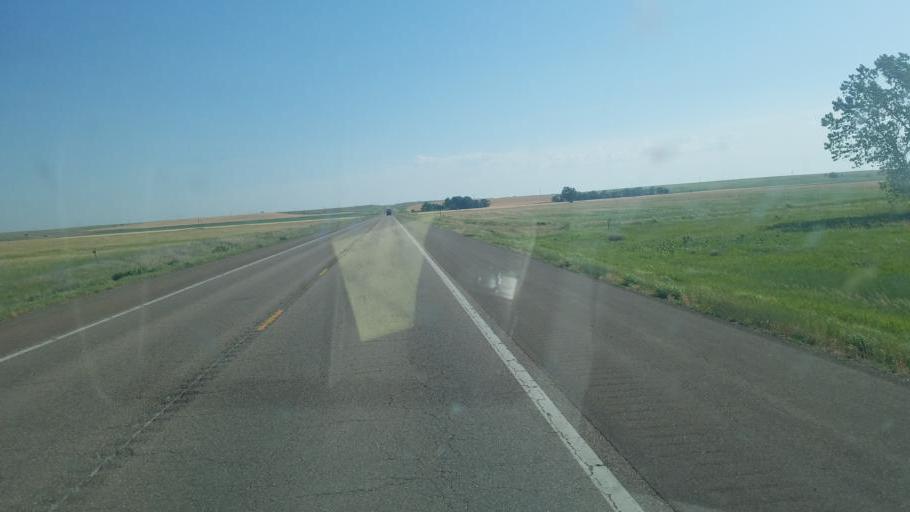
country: US
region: Kansas
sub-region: Barton County
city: Great Bend
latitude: 38.3730
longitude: -98.6898
